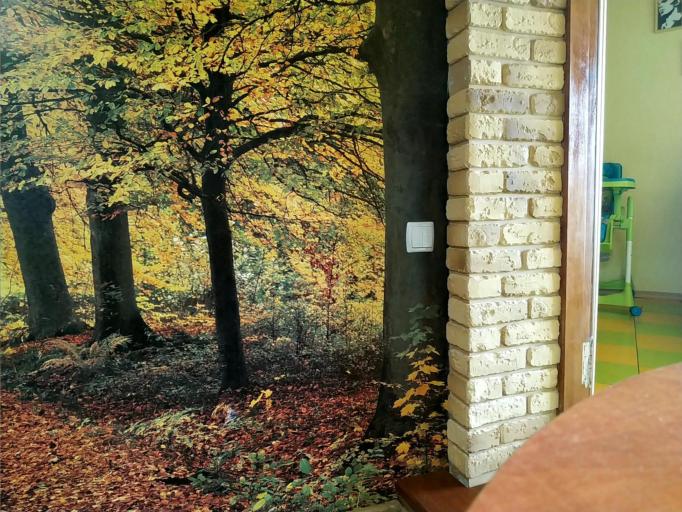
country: RU
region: Smolensk
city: Ozernyy
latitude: 55.4351
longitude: 32.7070
